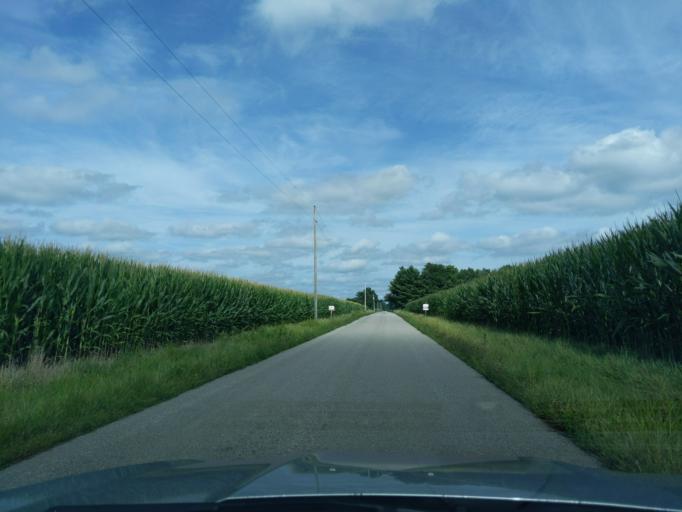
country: US
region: Indiana
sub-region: Decatur County
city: Greensburg
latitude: 39.2345
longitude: -85.4175
